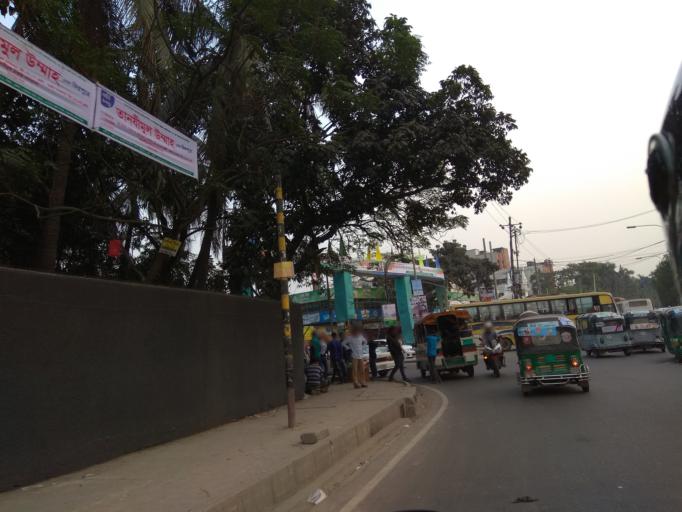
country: BD
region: Dhaka
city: Azimpur
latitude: 23.7736
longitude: 90.3671
